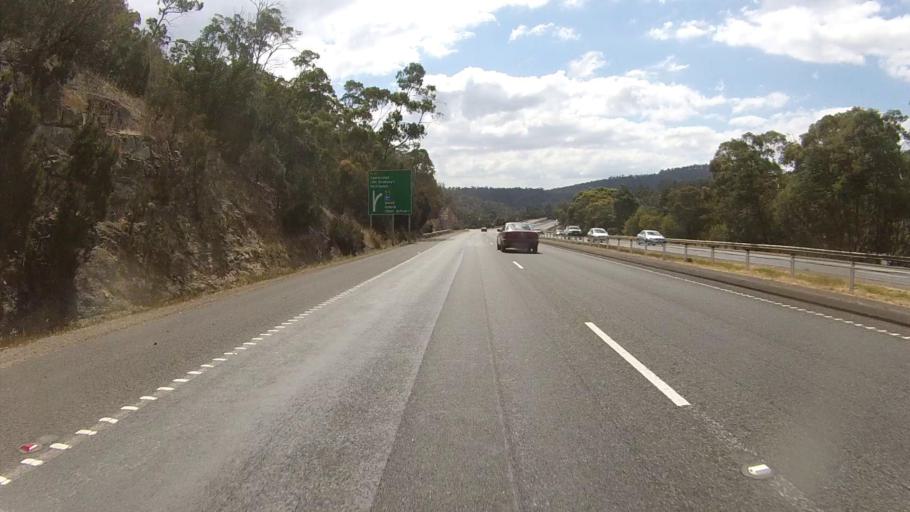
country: AU
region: Tasmania
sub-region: Clarence
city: Cambridge
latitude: -42.8491
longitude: 147.4193
